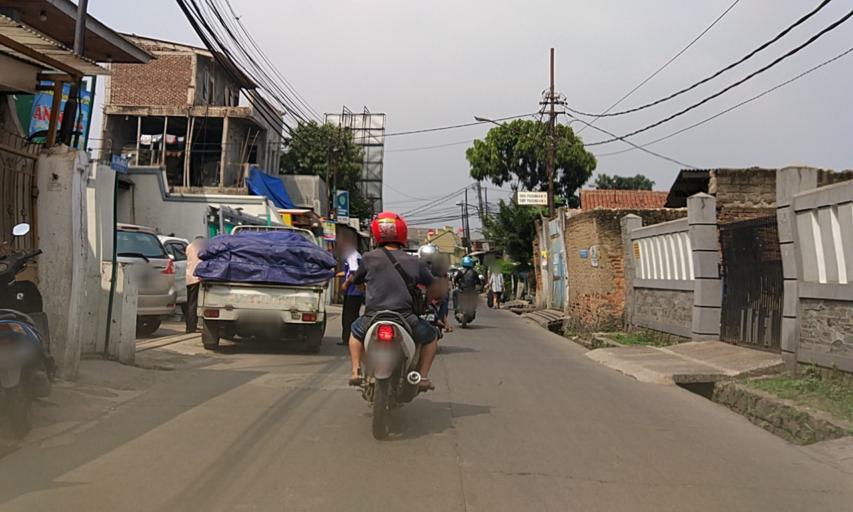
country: ID
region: West Java
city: Margahayukencana
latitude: -6.9422
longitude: 107.5843
